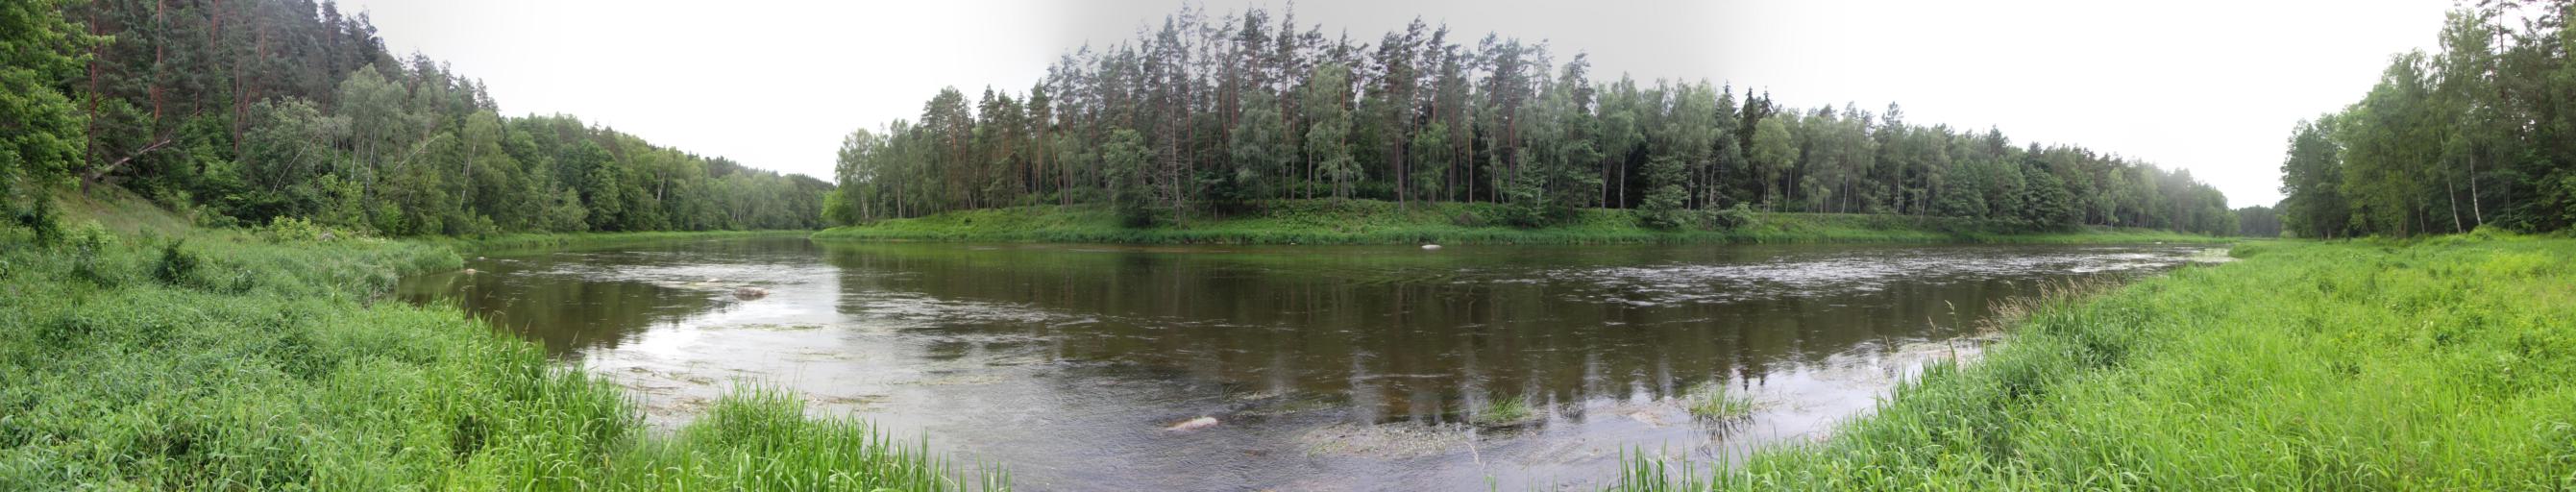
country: LT
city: Grigiskes
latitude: 54.8018
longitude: 24.9774
